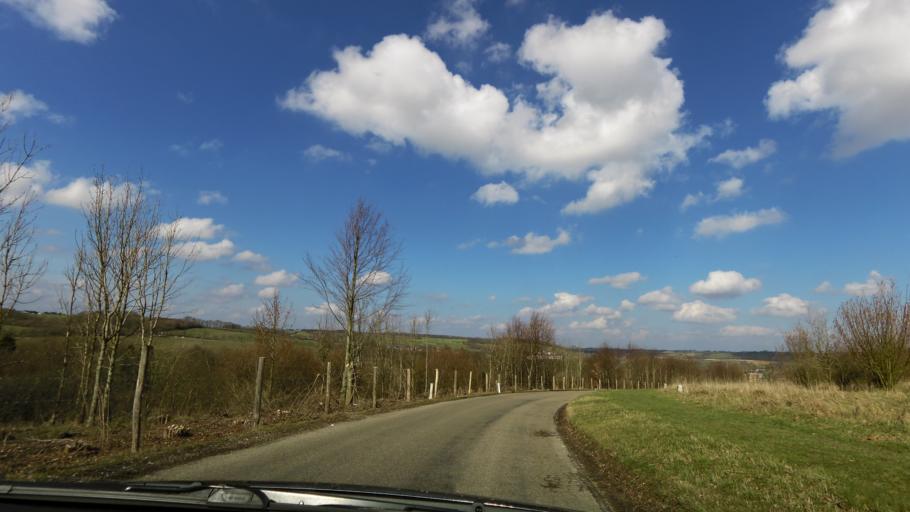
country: NL
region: Limburg
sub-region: Valkenburg aan de Geul
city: Schin op Geul
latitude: 50.8040
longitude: 5.8841
